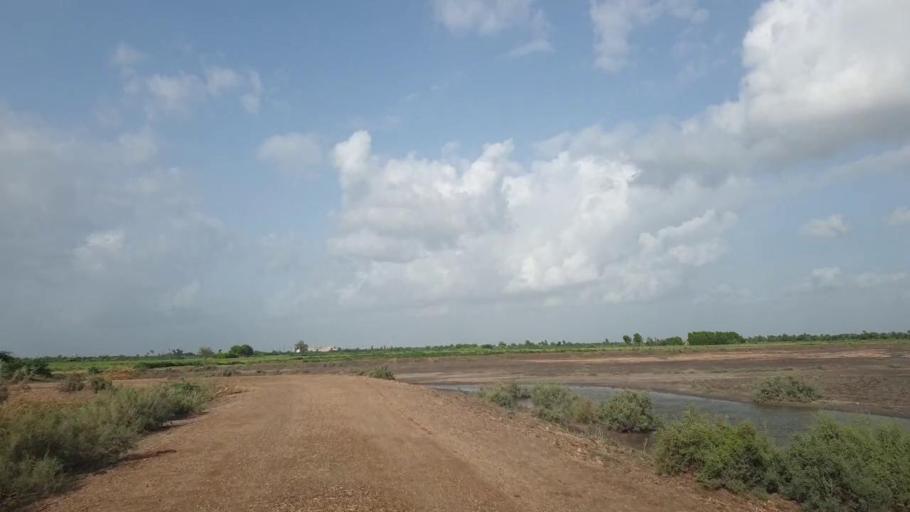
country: PK
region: Sindh
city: Kadhan
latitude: 24.6301
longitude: 69.0868
